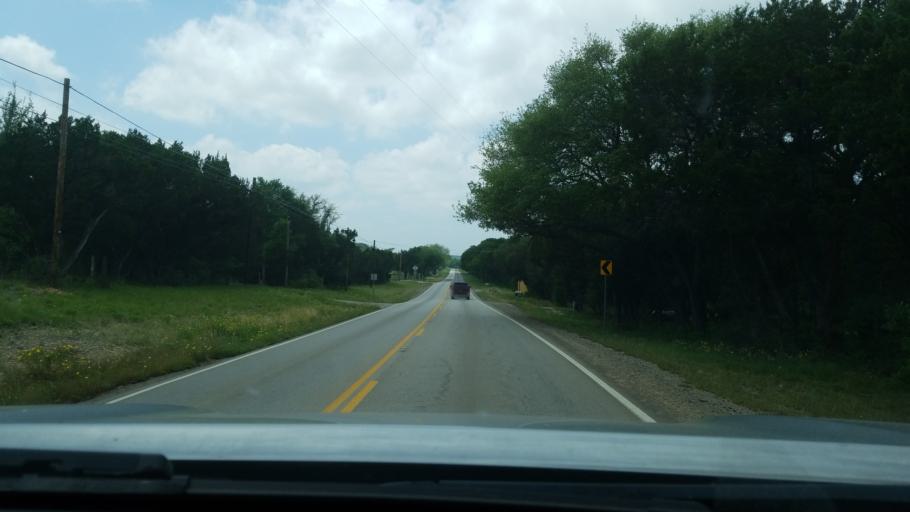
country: US
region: Texas
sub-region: Hays County
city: Dripping Springs
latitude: 30.1468
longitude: -98.0356
